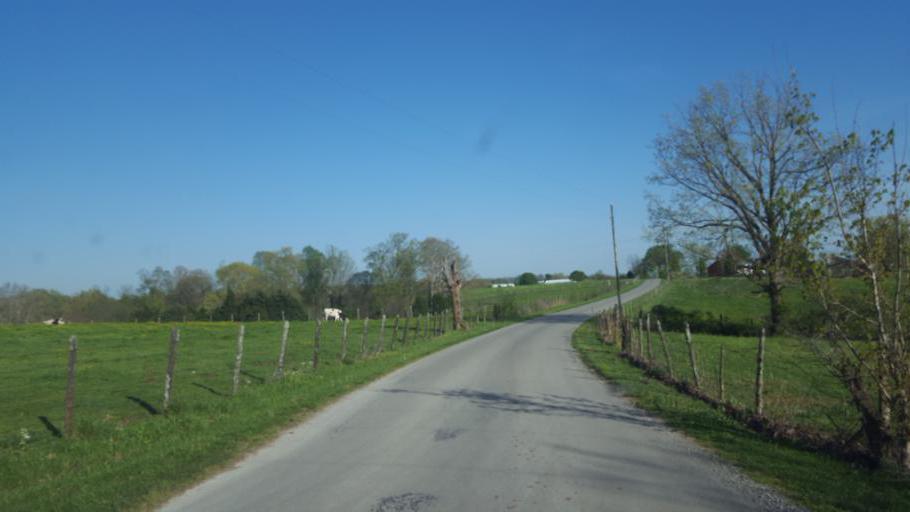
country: US
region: Kentucky
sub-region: Barren County
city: Cave City
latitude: 37.1721
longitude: -85.9903
